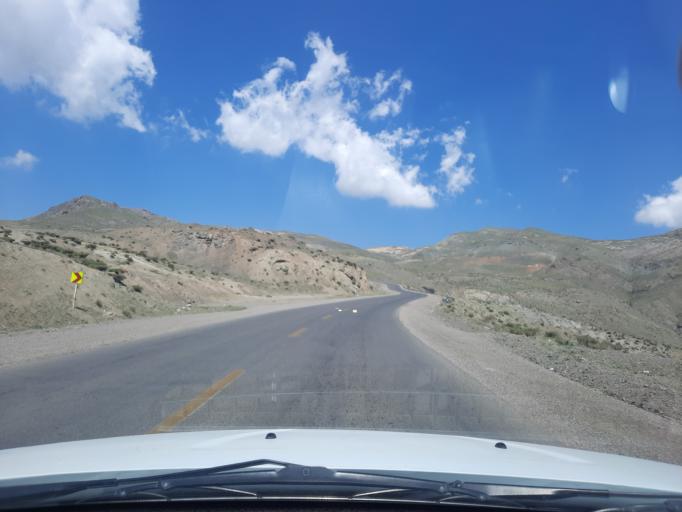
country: IR
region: Qazvin
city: Qazvin
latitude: 36.3601
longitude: 50.1953
